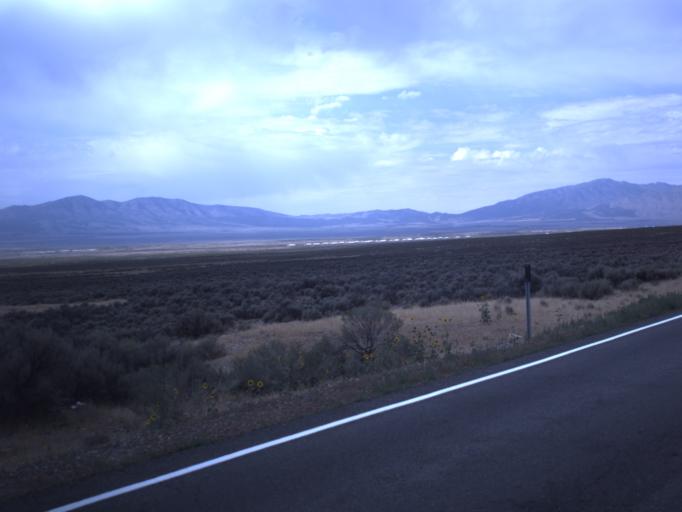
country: US
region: Utah
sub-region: Utah County
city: Eagle Mountain
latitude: 40.2805
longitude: -112.2574
